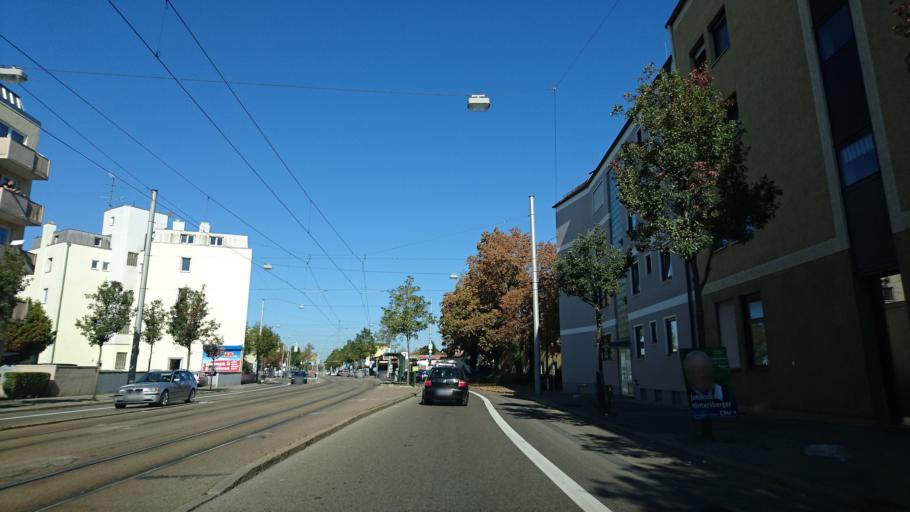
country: DE
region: Bavaria
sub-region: Swabia
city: Augsburg
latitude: 48.3878
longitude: 10.8812
